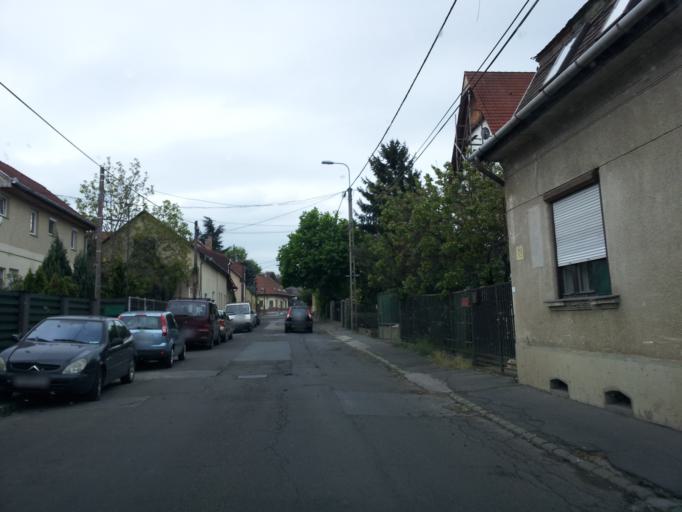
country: HU
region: Budapest
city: Budapest XI. keruelet
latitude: 47.4524
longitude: 19.0211
